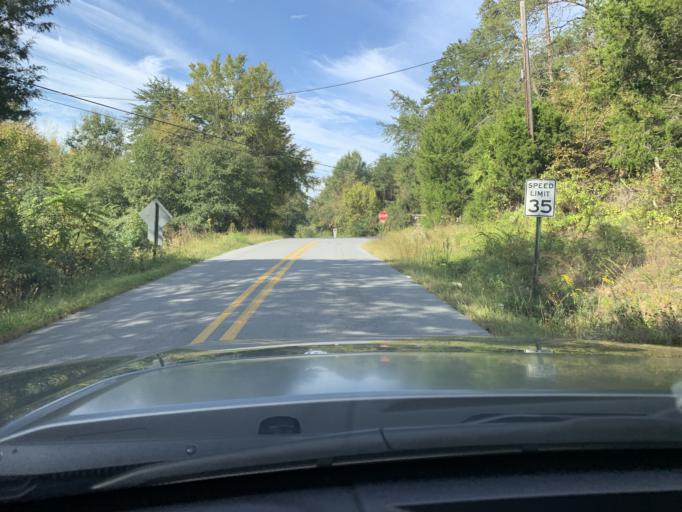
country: US
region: Georgia
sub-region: Polk County
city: Aragon
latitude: 34.0320
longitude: -85.0257
